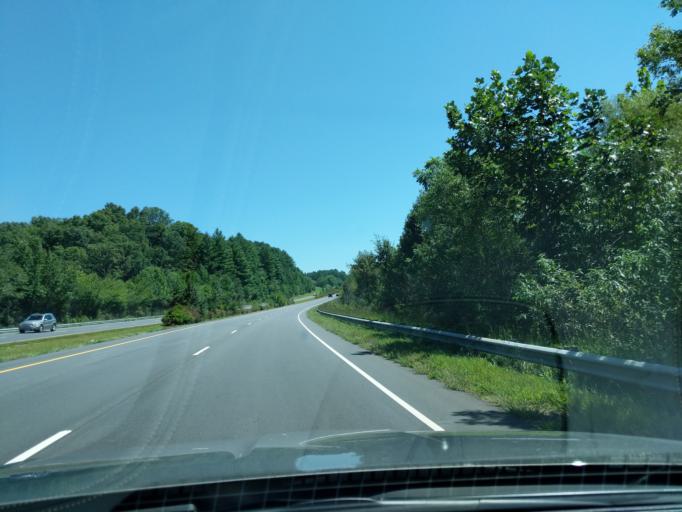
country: US
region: North Carolina
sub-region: Macon County
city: Franklin
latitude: 35.1653
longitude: -83.4320
